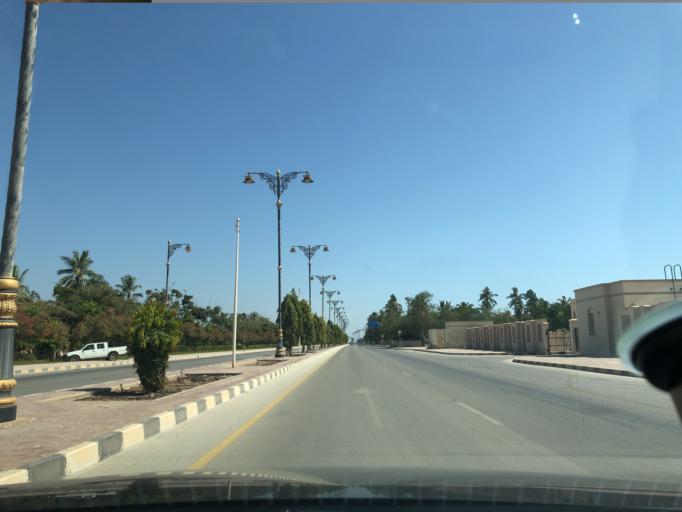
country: OM
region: Zufar
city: Salalah
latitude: 17.0260
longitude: 54.1516
